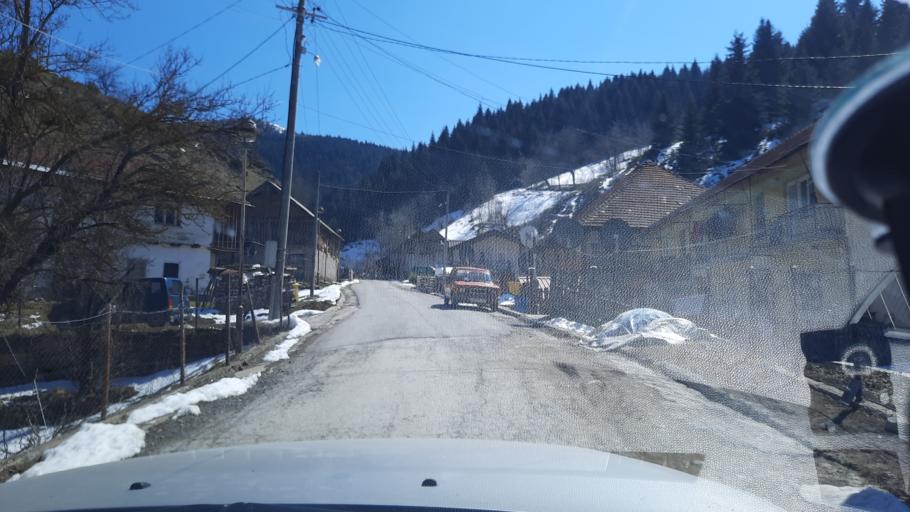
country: MK
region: Gostivar
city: Vrutok
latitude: 41.7207
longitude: 20.7330
